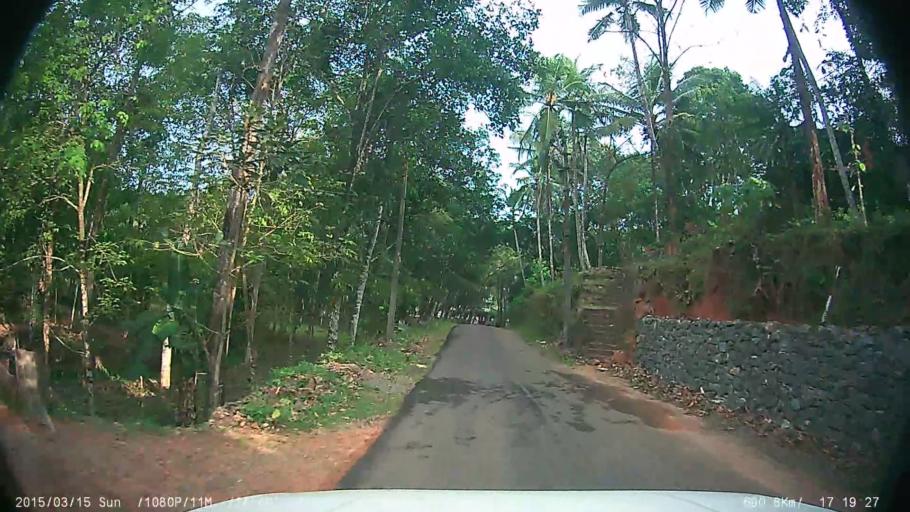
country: IN
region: Kerala
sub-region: Kottayam
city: Palackattumala
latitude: 9.8496
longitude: 76.7003
